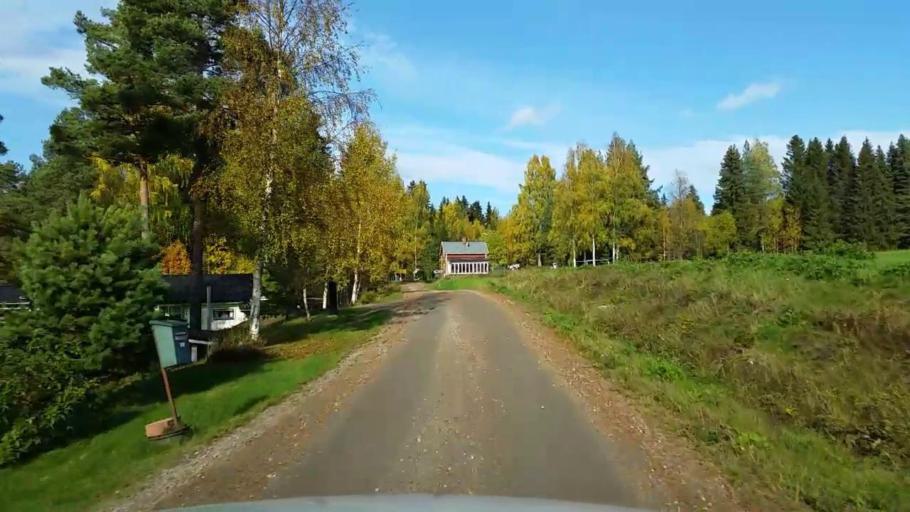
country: SE
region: Gaevleborg
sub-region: Ljusdals Kommun
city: Jaervsoe
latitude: 61.7857
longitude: 16.1534
